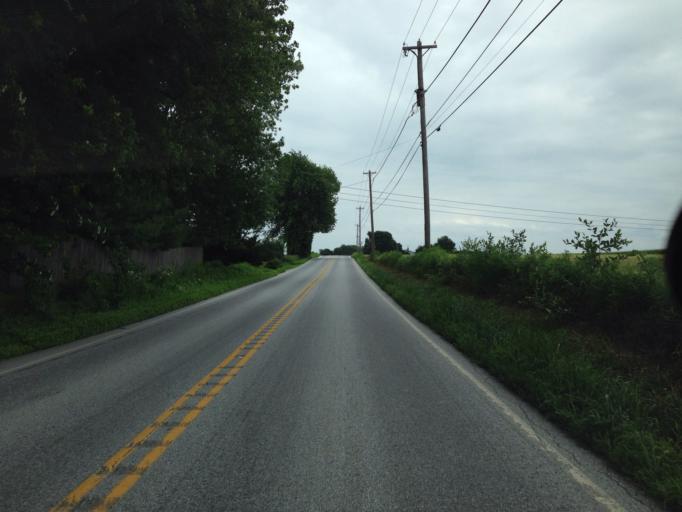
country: US
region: Pennsylvania
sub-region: Chester County
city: Oxford
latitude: 39.8534
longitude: -75.9657
